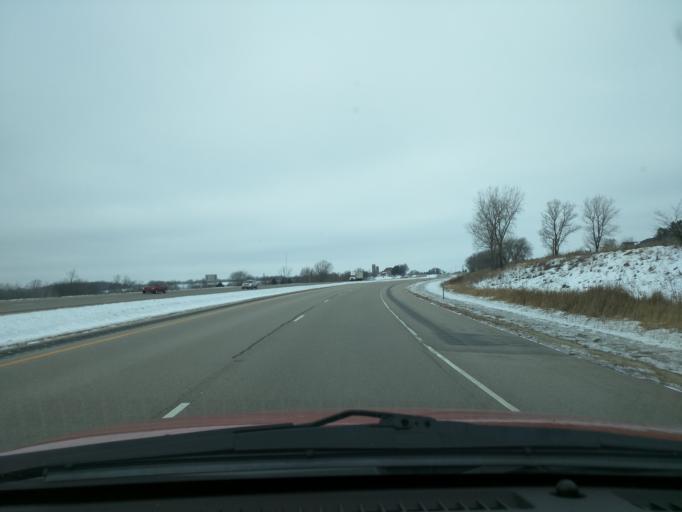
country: US
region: Wisconsin
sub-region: Trempealeau County
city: Trempealeau
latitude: 43.9106
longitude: -91.5612
